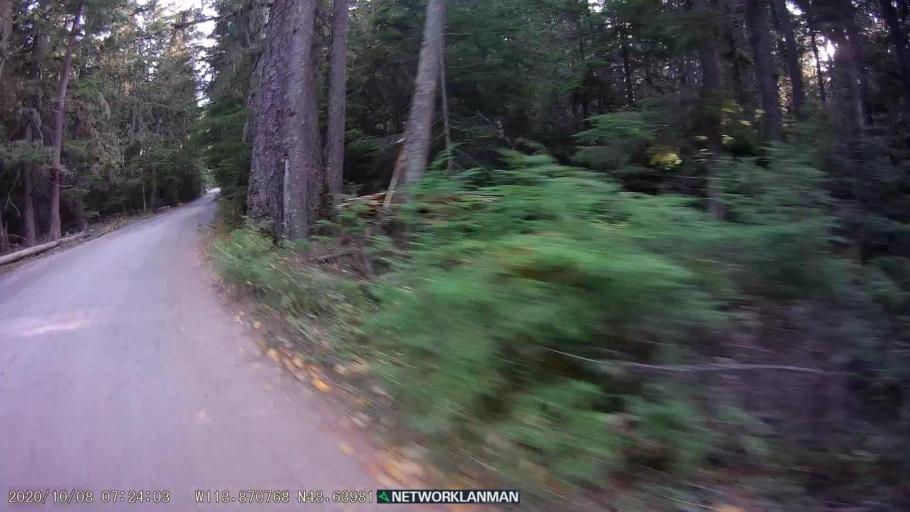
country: US
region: Montana
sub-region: Flathead County
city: Columbia Falls
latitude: 48.6397
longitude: -113.8707
